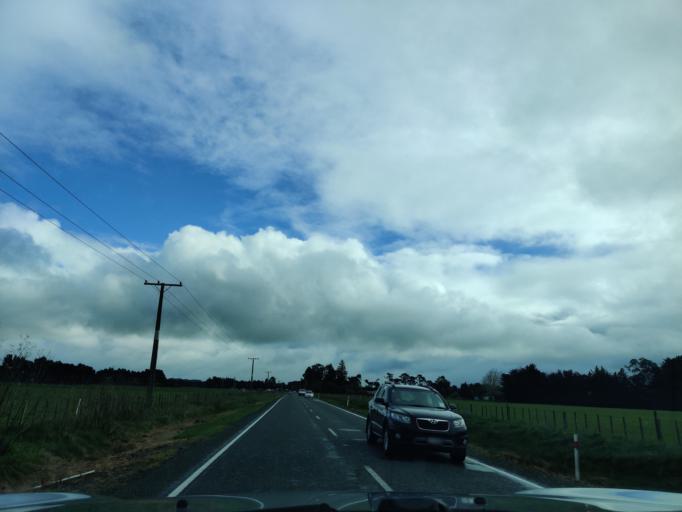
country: NZ
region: Hawke's Bay
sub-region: Hastings District
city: Hastings
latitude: -40.0194
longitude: 176.3427
